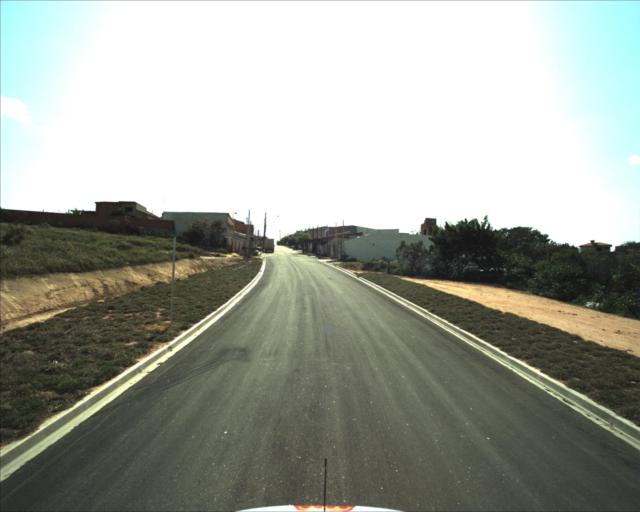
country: BR
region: Sao Paulo
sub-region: Sorocaba
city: Sorocaba
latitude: -23.4394
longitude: -47.4875
